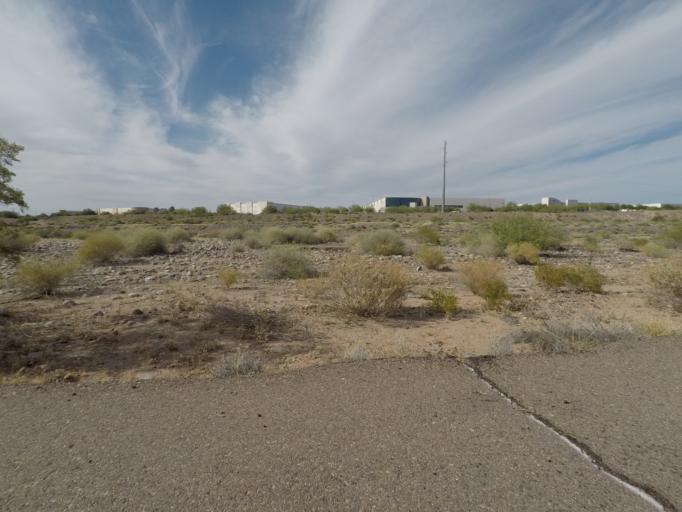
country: US
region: Arizona
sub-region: Maricopa County
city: Phoenix
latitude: 33.4167
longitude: -112.0449
